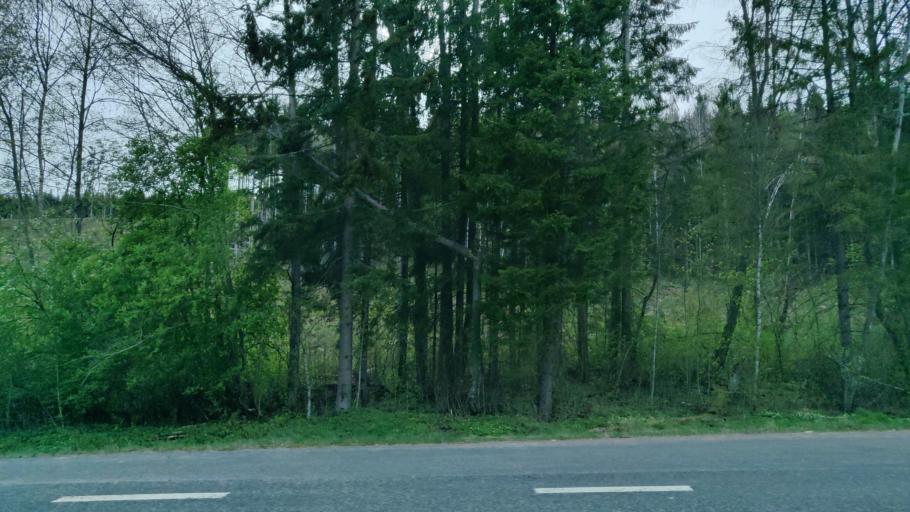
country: SE
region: Vaermland
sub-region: Munkfors Kommun
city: Munkfors
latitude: 59.7671
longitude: 13.4387
